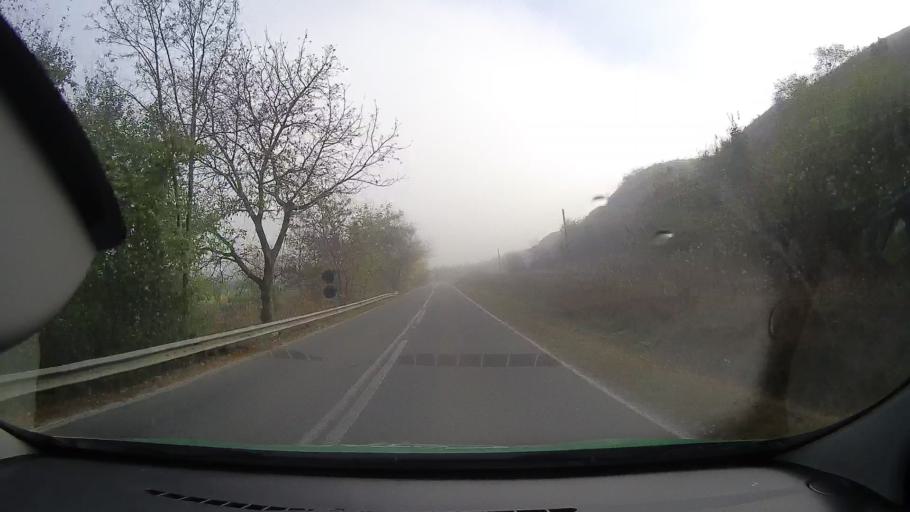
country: RO
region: Tulcea
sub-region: Comuna Nufaru
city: Nufaru
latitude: 45.1467
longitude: 28.9107
